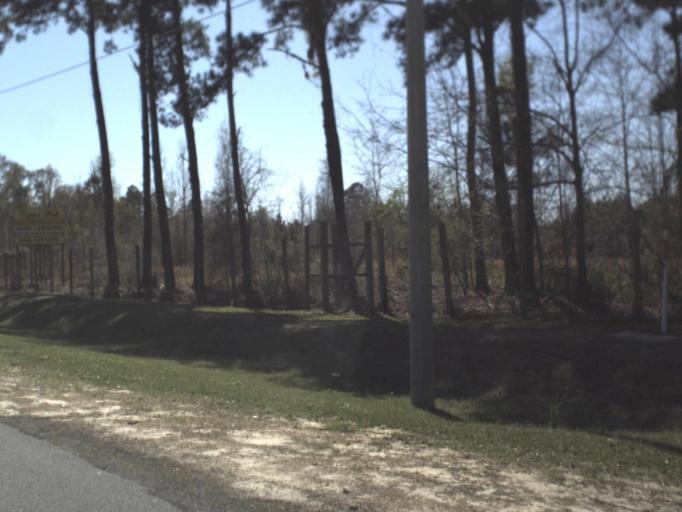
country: US
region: Florida
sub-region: Gadsden County
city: Midway
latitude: 30.4831
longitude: -84.3633
